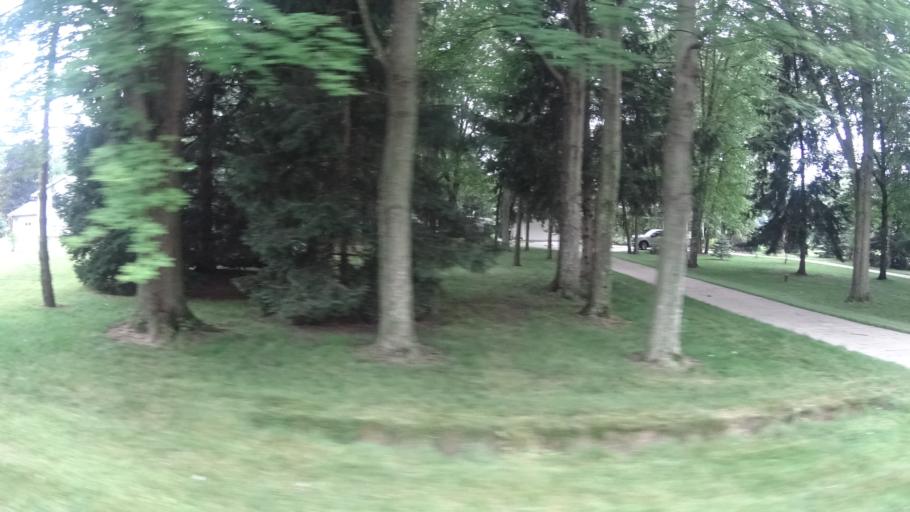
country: US
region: Ohio
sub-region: Erie County
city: Milan
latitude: 41.2983
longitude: -82.5352
